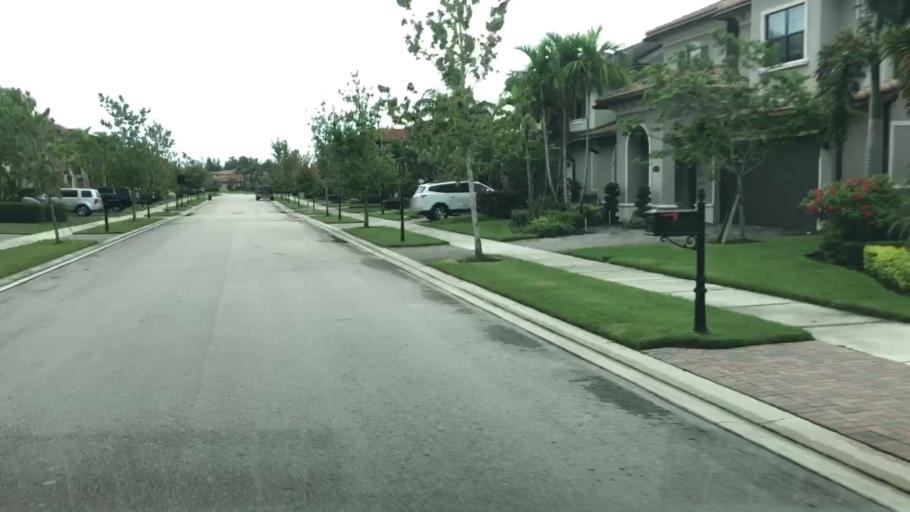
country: US
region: Florida
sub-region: Broward County
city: Parkland
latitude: 26.3437
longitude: -80.2797
